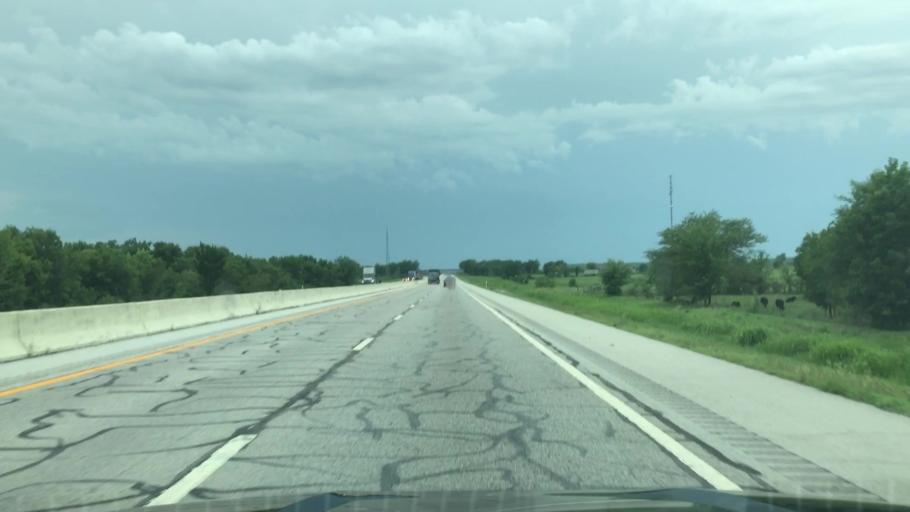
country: US
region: Oklahoma
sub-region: Rogers County
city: Chelsea
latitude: 36.5134
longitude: -95.2674
